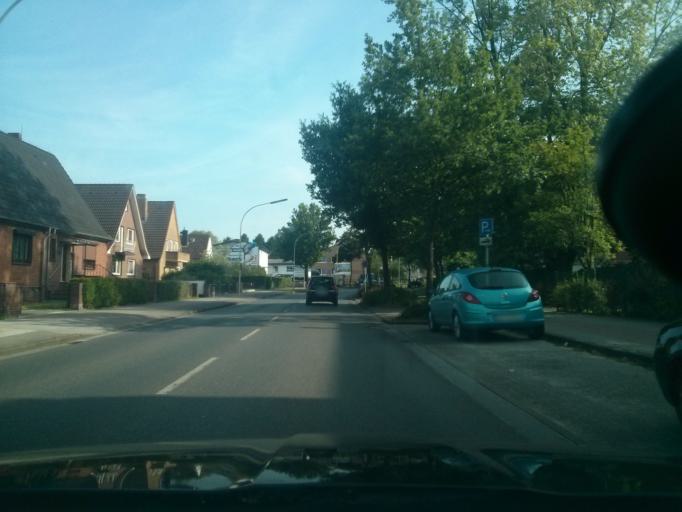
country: DE
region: Schleswig-Holstein
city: Halstenbek
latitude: 53.5995
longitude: 9.8380
